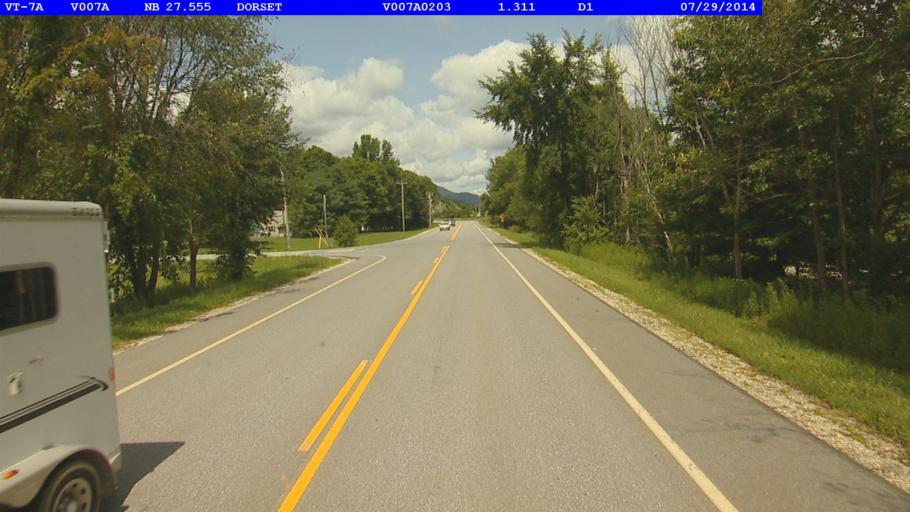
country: US
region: Vermont
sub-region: Bennington County
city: Manchester Center
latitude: 43.2284
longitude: -73.0112
